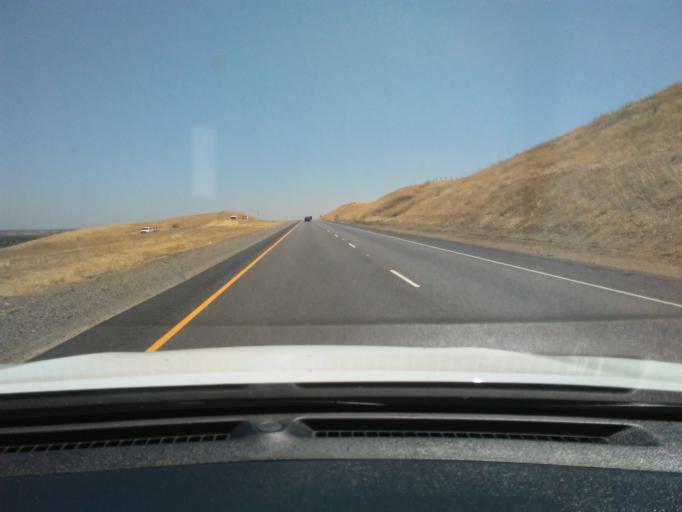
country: US
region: California
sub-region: Stanislaus County
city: Patterson
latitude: 37.4349
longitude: -121.1602
